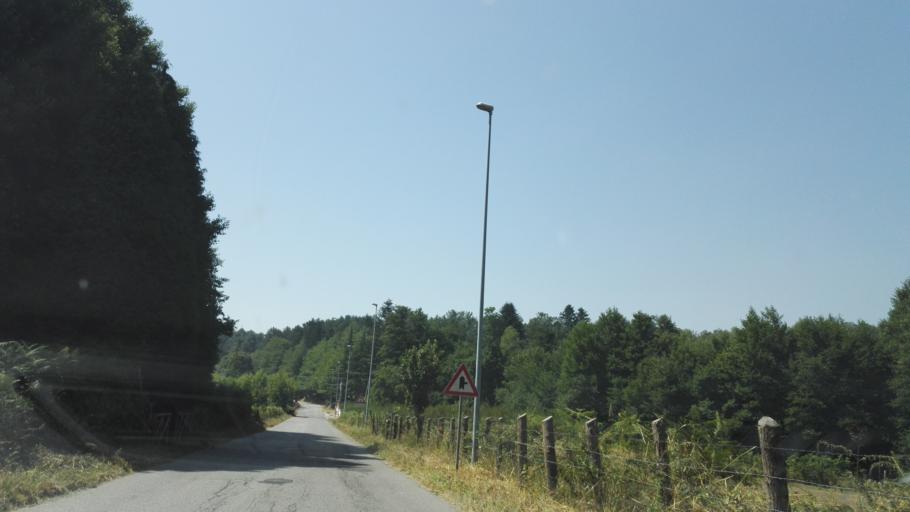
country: IT
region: Calabria
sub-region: Provincia di Vibo-Valentia
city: Mongiana
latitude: 38.5265
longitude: 16.3203
